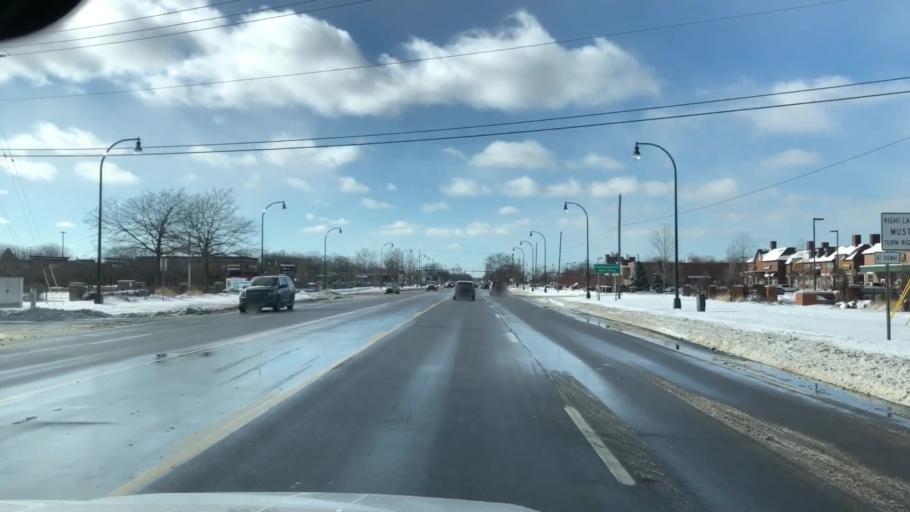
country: US
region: Michigan
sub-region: Wayne County
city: Livonia
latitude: 42.3684
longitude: -83.3685
